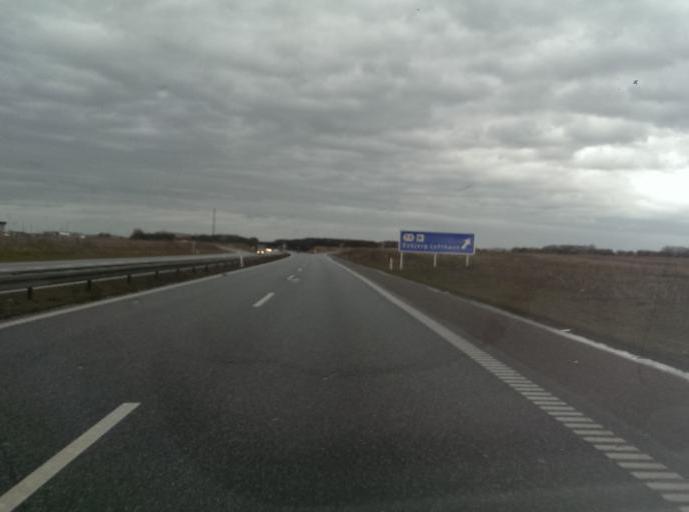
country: DK
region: South Denmark
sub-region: Esbjerg Kommune
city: Tjaereborg
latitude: 55.5178
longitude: 8.5378
